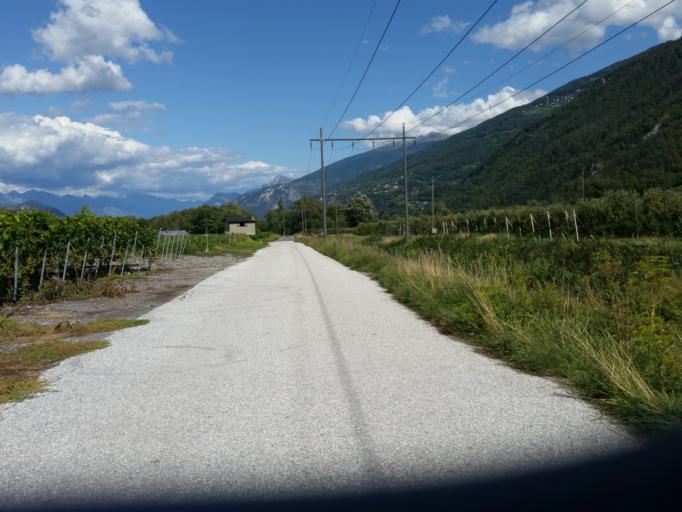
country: CH
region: Valais
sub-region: Conthey District
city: Ardon
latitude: 46.2004
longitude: 7.2733
